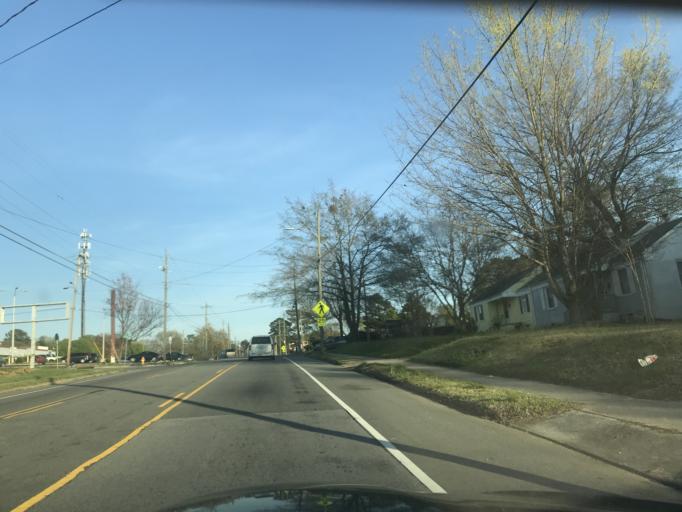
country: US
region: North Carolina
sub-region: Wake County
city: Raleigh
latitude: 35.7771
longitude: -78.6123
